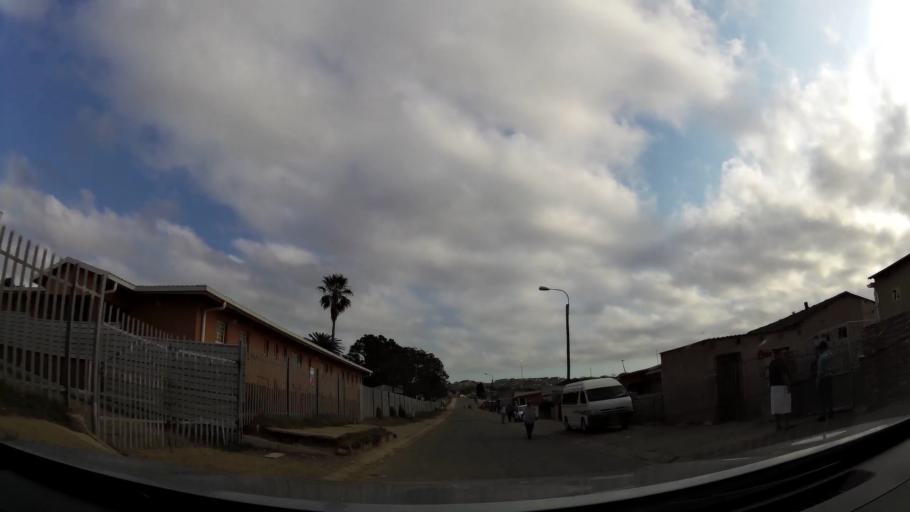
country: ZA
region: Eastern Cape
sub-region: Nelson Mandela Bay Metropolitan Municipality
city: Port Elizabeth
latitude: -33.9153
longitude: 25.5475
